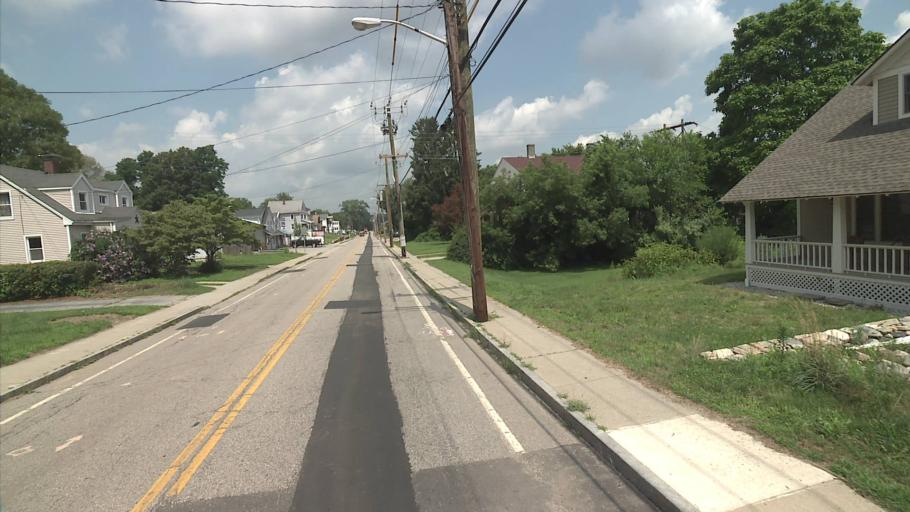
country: US
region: Connecticut
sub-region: New London County
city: Jewett City
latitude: 41.5989
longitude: -71.9798
